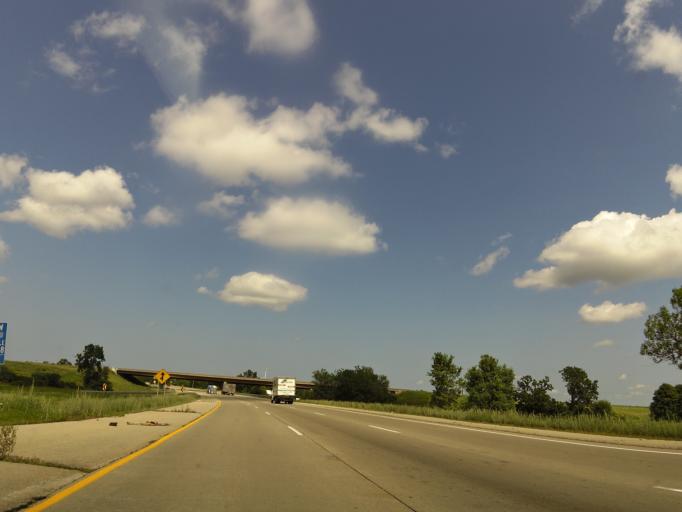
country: US
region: Wisconsin
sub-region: Dane County
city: Monona
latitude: 43.1018
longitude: -89.2829
